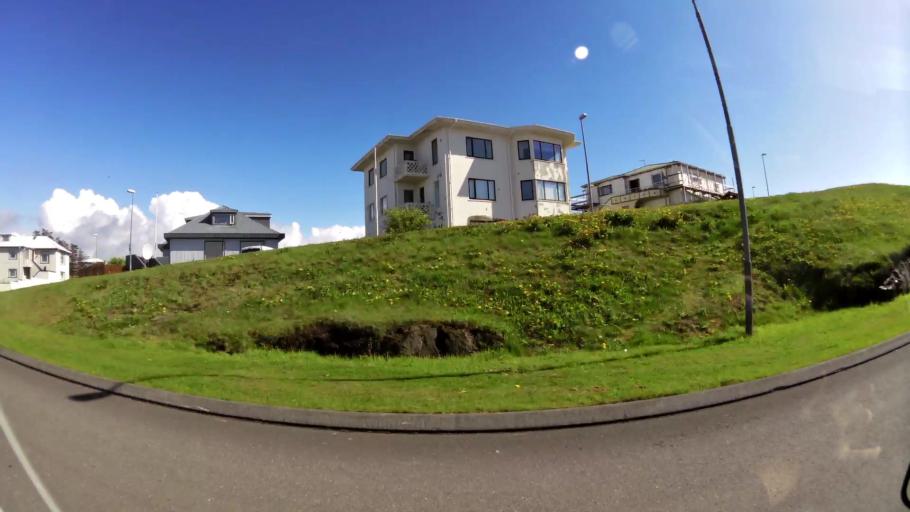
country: IS
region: East
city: Hoefn
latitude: 64.2500
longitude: -15.2082
